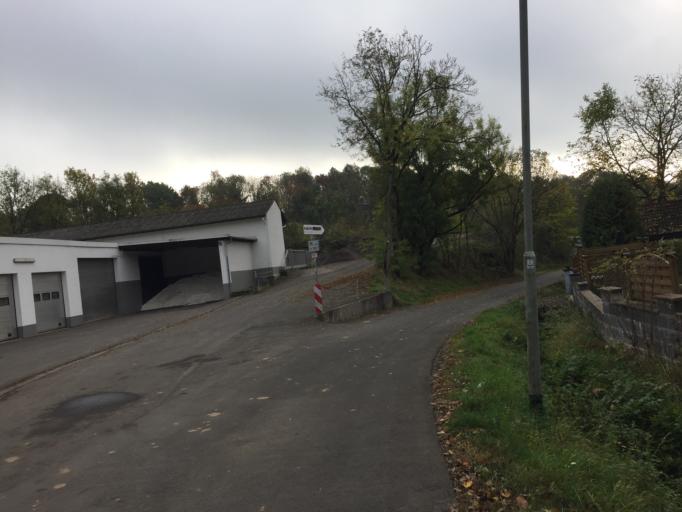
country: DE
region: Hesse
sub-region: Regierungsbezirk Giessen
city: Grunberg
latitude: 50.5971
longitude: 8.9627
